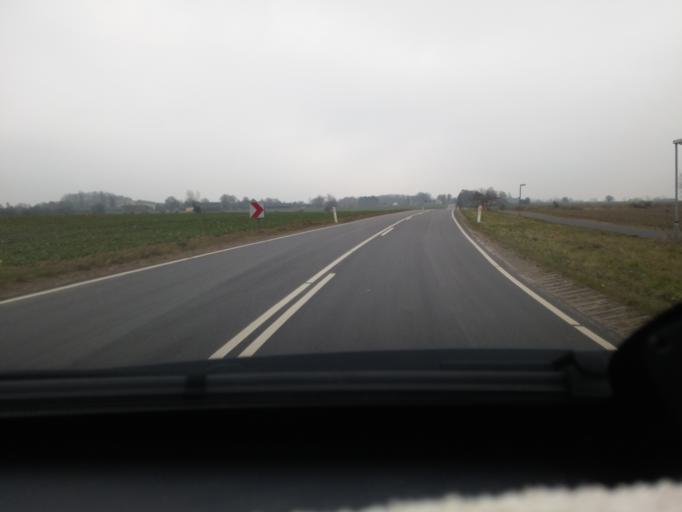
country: DK
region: South Denmark
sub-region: Nyborg Kommune
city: Ullerslev
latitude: 55.3755
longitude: 10.7274
